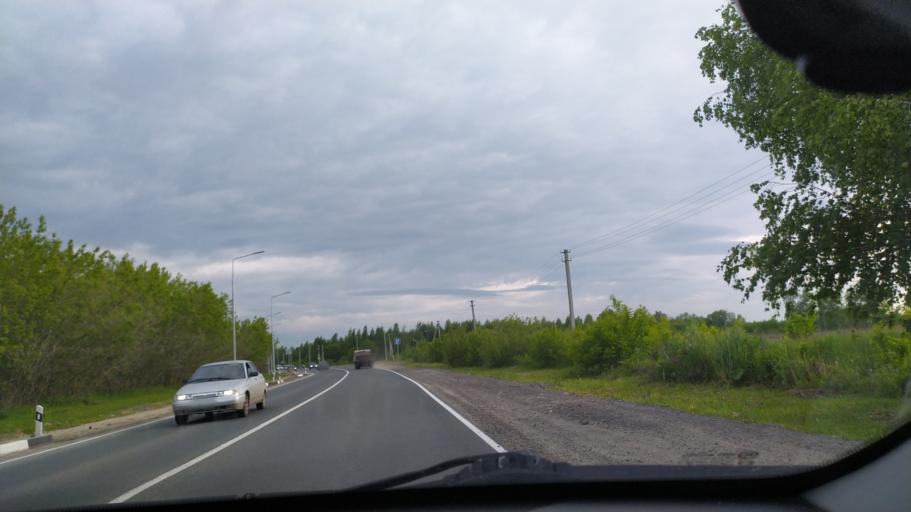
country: RU
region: Chuvashia
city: Novyye Lapsary
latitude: 56.1065
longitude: 47.2132
